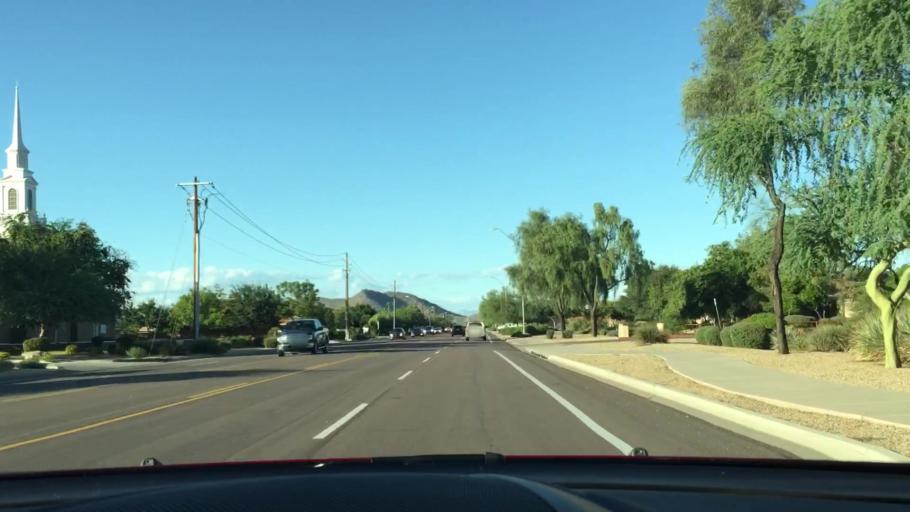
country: US
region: Arizona
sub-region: Maricopa County
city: Sun City
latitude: 33.6832
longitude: -112.2377
